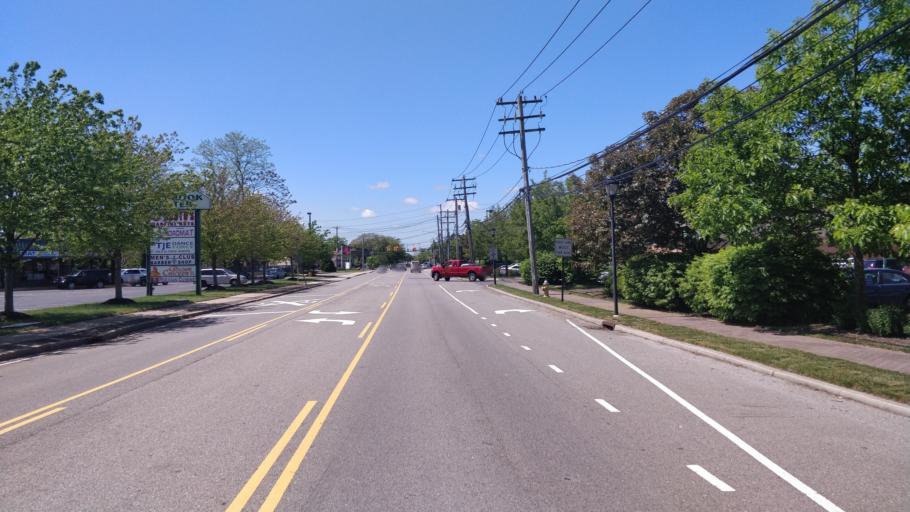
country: US
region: New York
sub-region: Suffolk County
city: Holbrook
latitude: 40.8109
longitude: -73.0786
